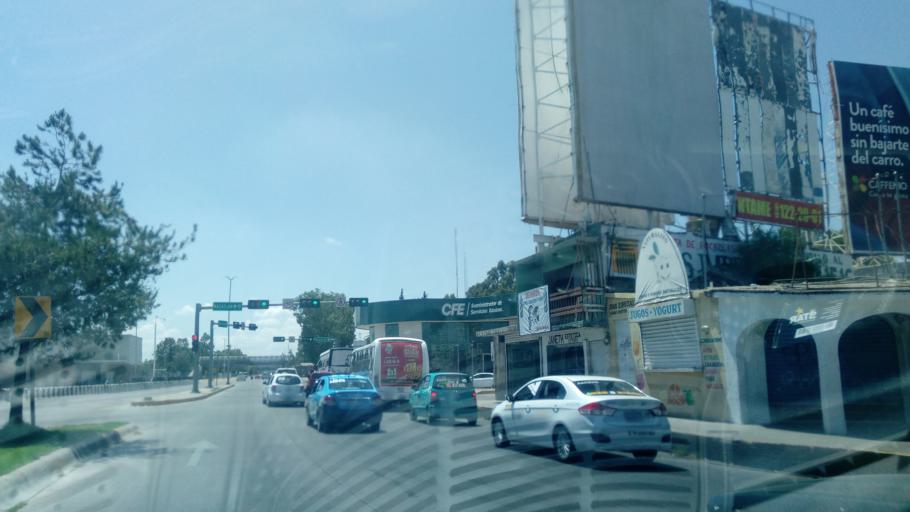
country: MX
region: Durango
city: Victoria de Durango
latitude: 24.0333
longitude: -104.6397
